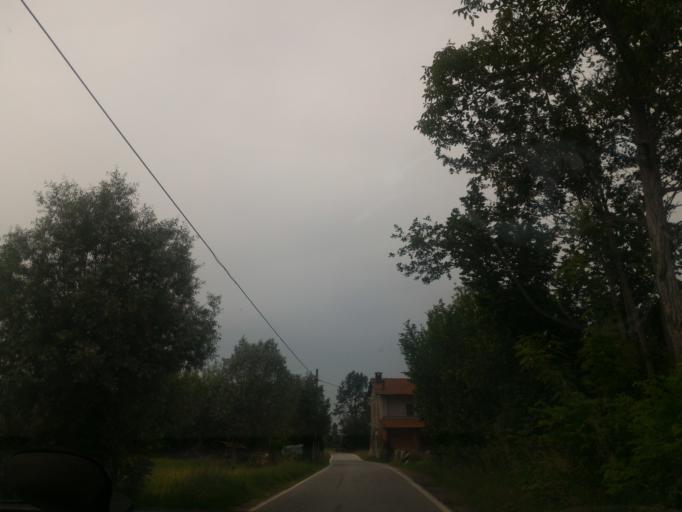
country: IT
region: Piedmont
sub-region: Provincia di Cuneo
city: Beinette
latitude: 44.3643
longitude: 7.6141
